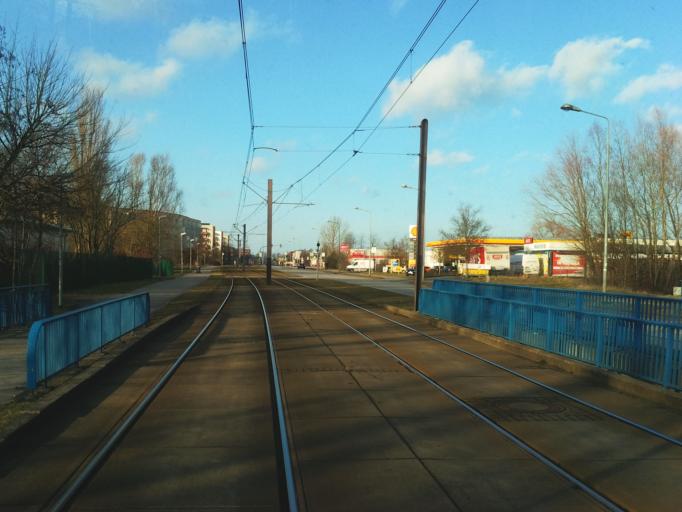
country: DE
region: Mecklenburg-Vorpommern
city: Lambrechtshagen
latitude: 54.1297
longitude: 12.0574
